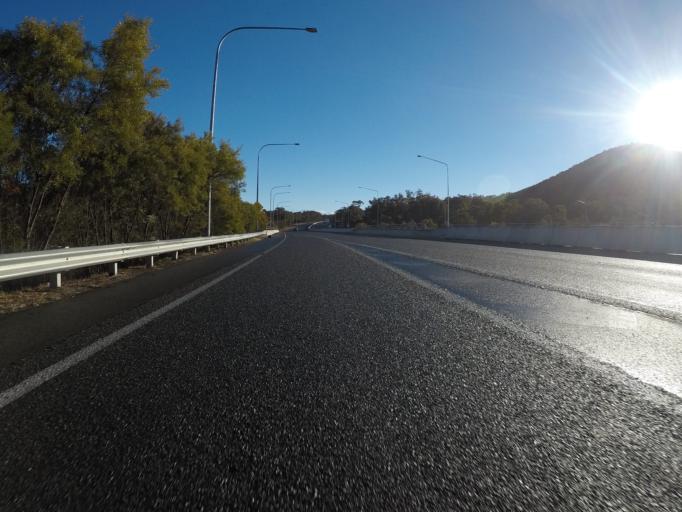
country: AU
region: Australian Capital Territory
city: Acton
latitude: -35.2811
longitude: 149.0862
